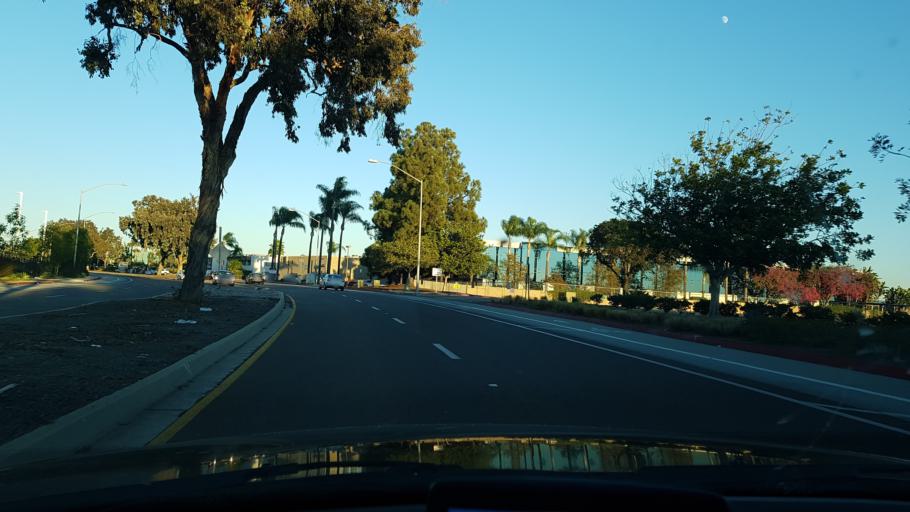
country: US
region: California
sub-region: San Diego County
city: San Diego
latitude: 32.8202
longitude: -117.1402
